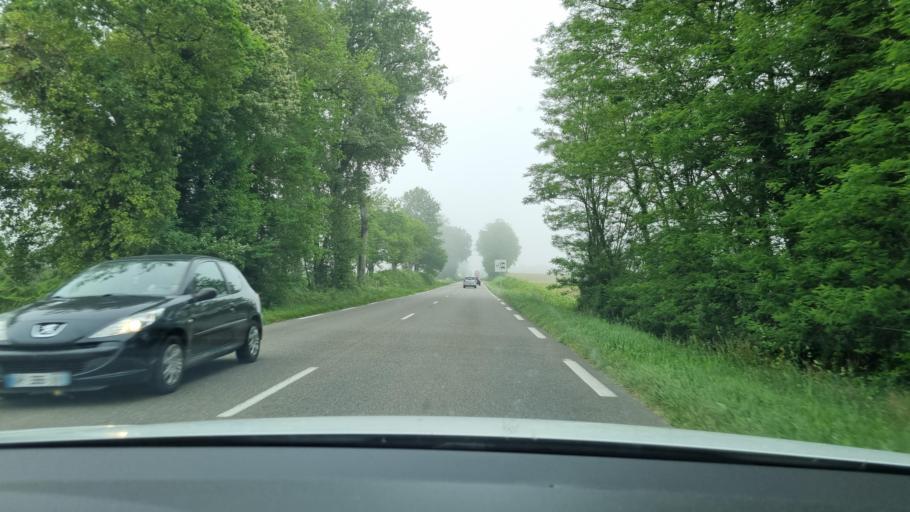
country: FR
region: Aquitaine
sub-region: Departement des Landes
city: Hagetmau
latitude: 43.6259
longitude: -0.6254
